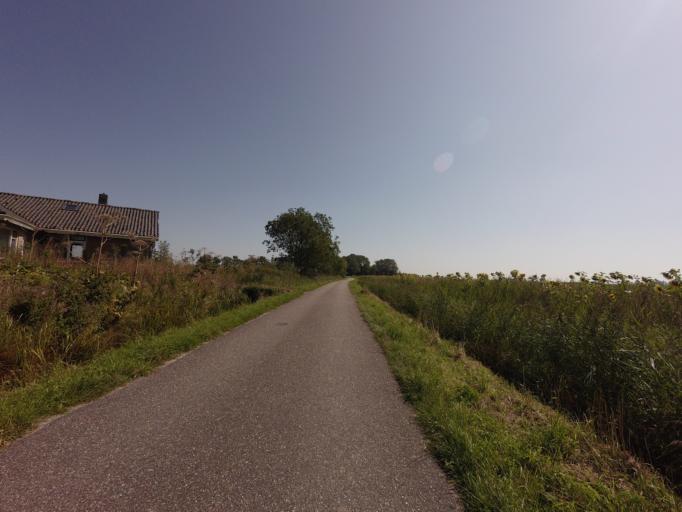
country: NL
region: Friesland
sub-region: Gemeente Dongeradeel
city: Holwerd
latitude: 53.3674
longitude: 5.9092
